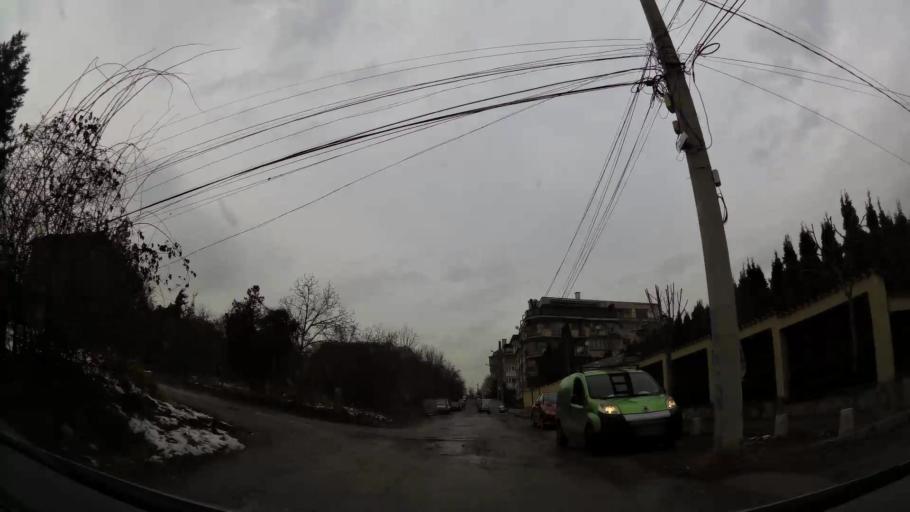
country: BG
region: Sofia-Capital
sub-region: Stolichna Obshtina
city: Sofia
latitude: 42.6676
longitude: 23.2461
